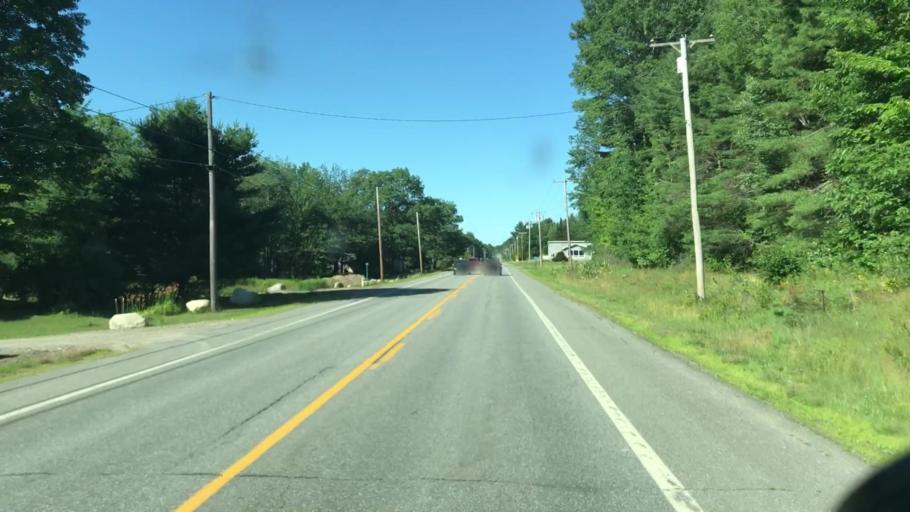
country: US
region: Maine
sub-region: Penobscot County
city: Lincoln
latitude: 45.3378
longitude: -68.5743
